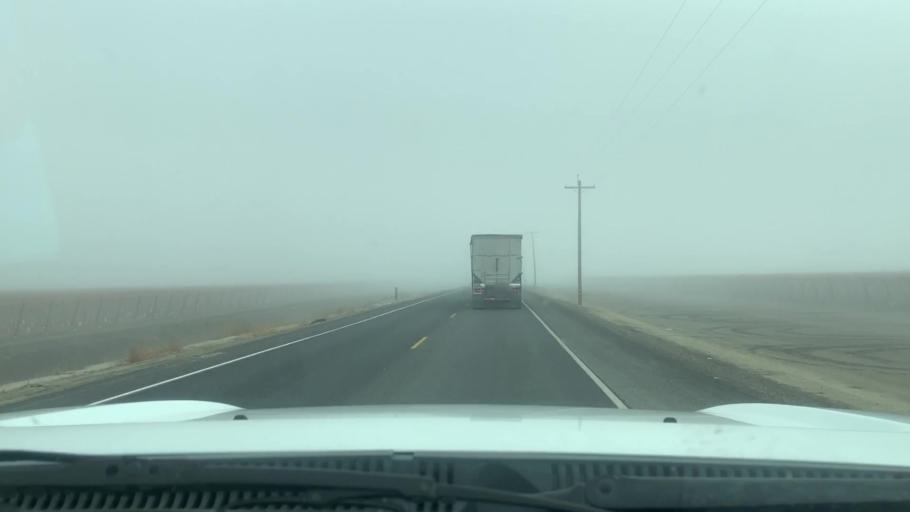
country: US
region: California
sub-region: Kern County
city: Lost Hills
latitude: 35.4994
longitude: -119.5908
